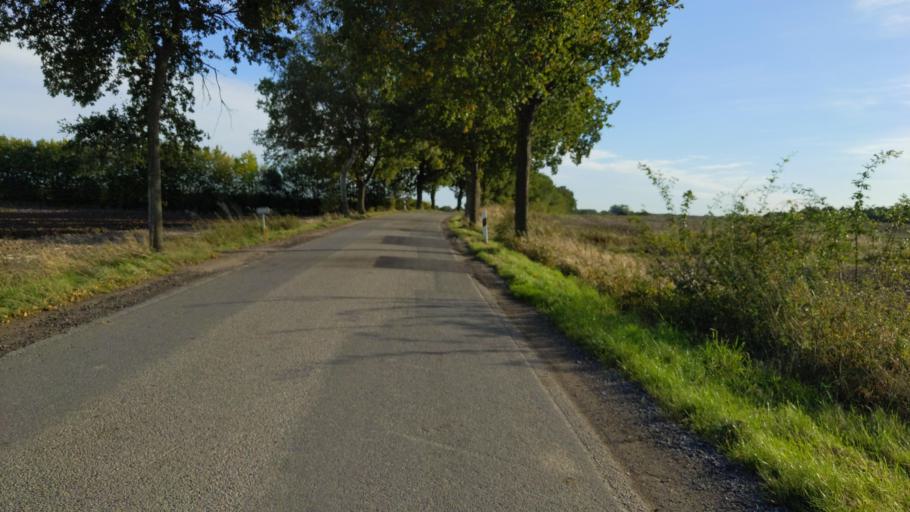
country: DE
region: Schleswig-Holstein
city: Ahrensbok
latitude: 54.0489
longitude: 10.5998
